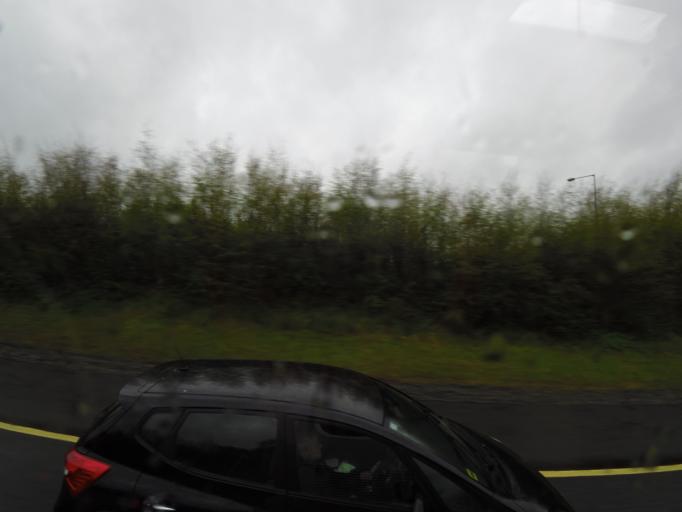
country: IE
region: Leinster
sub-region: Kildare
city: Maynooth
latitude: 53.3667
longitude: -6.5891
